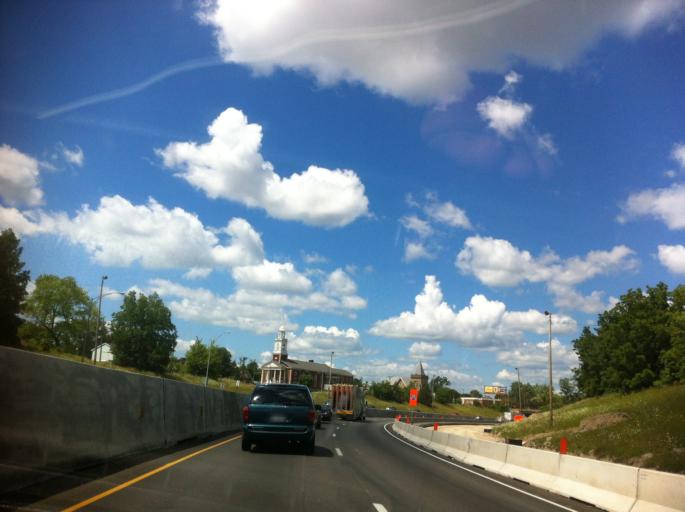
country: US
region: Ohio
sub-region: Lucas County
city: Toledo
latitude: 41.6583
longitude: -83.5626
